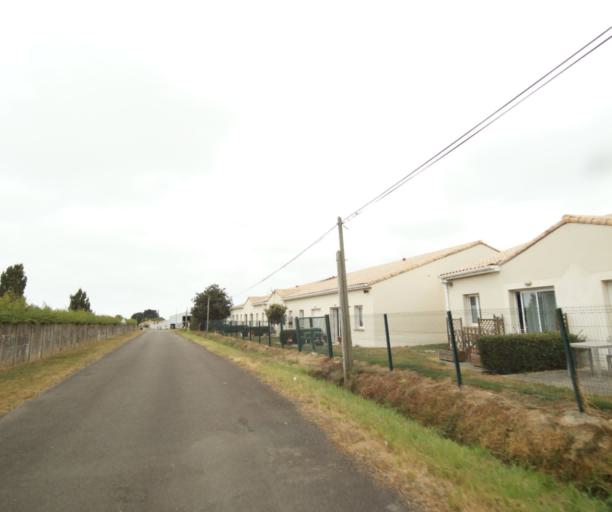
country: FR
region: Pays de la Loire
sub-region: Departement de la Vendee
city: Chateau-d'Olonne
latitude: 46.5032
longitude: -1.7274
